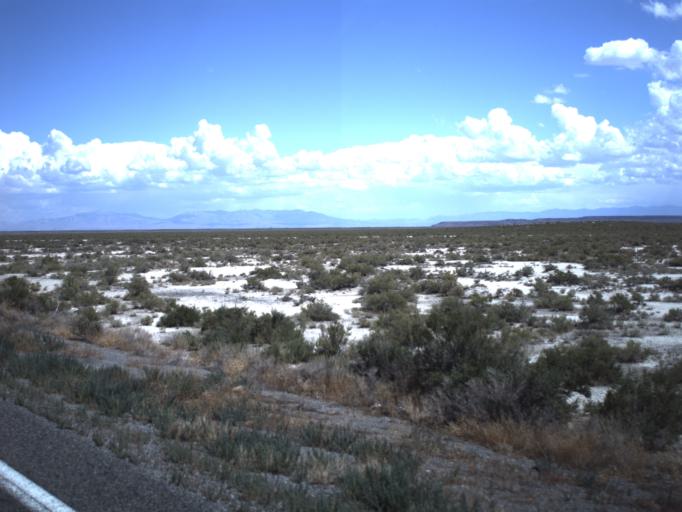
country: US
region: Utah
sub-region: Millard County
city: Delta
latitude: 39.2544
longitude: -112.8905
